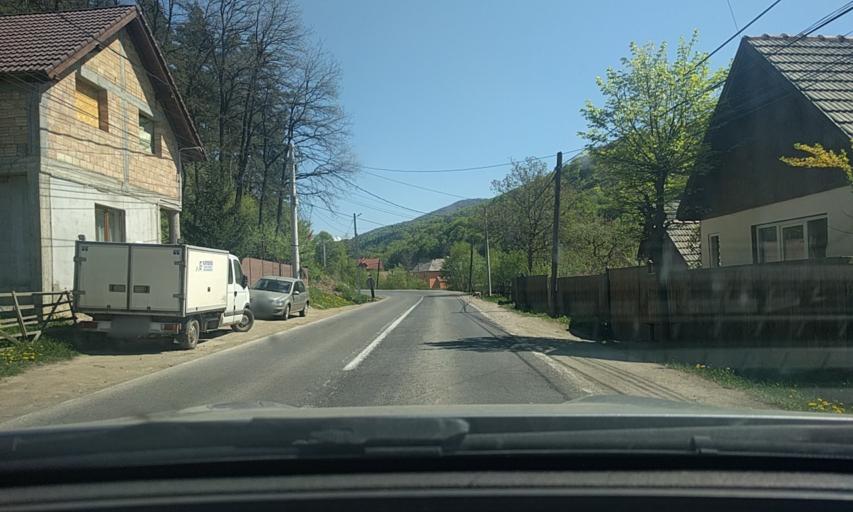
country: RO
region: Brasov
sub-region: Comuna Teliu
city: Teliu
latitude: 45.6955
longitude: 25.8673
